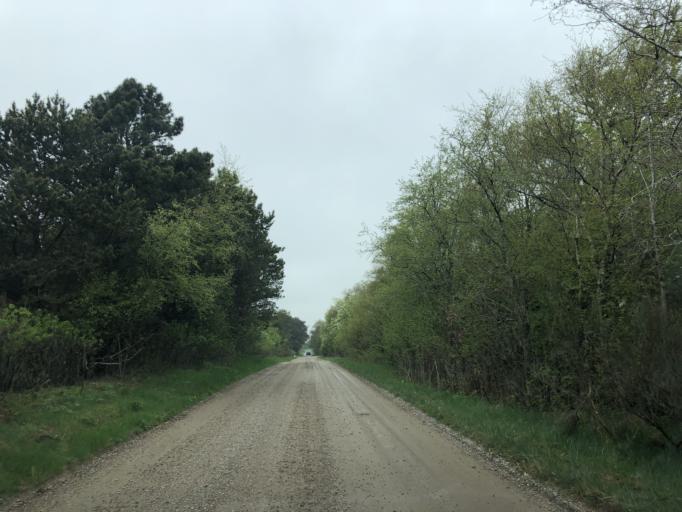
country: DK
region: Central Jutland
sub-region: Lemvig Kommune
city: Lemvig
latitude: 56.5101
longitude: 8.3173
